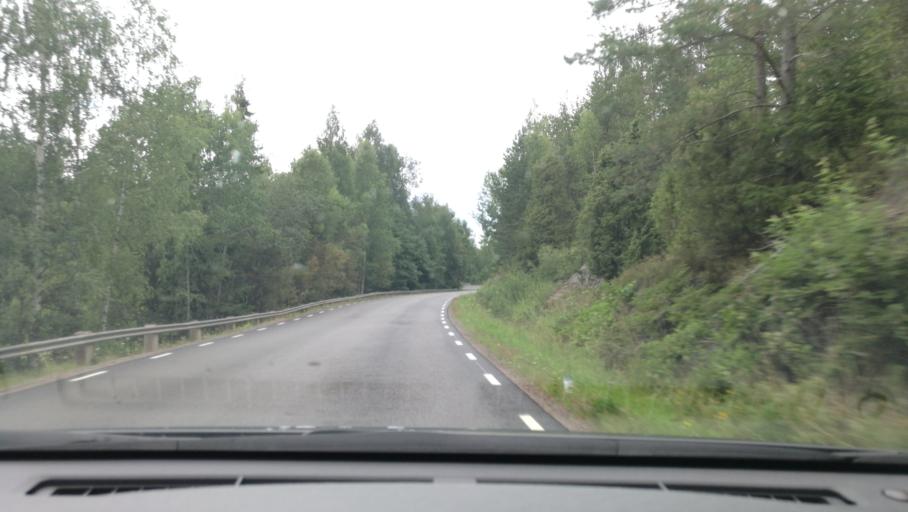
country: SE
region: OEstergoetland
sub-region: Norrkopings Kommun
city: Jursla
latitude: 58.8094
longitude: 16.0989
